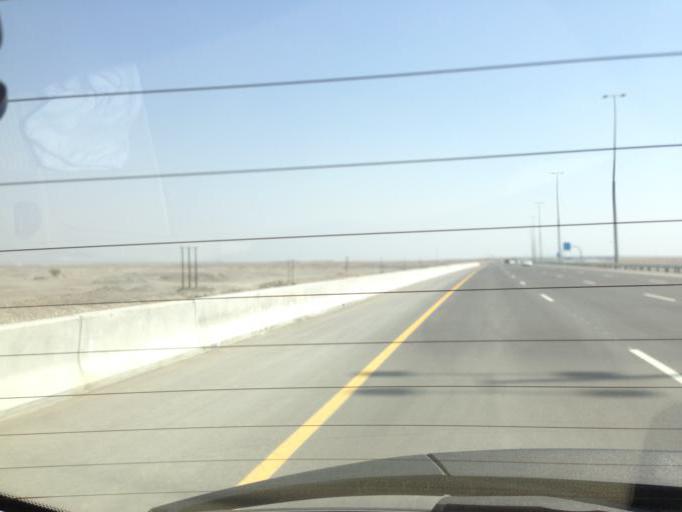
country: OM
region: Al Batinah
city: Barka'
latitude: 23.5690
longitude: 57.7101
